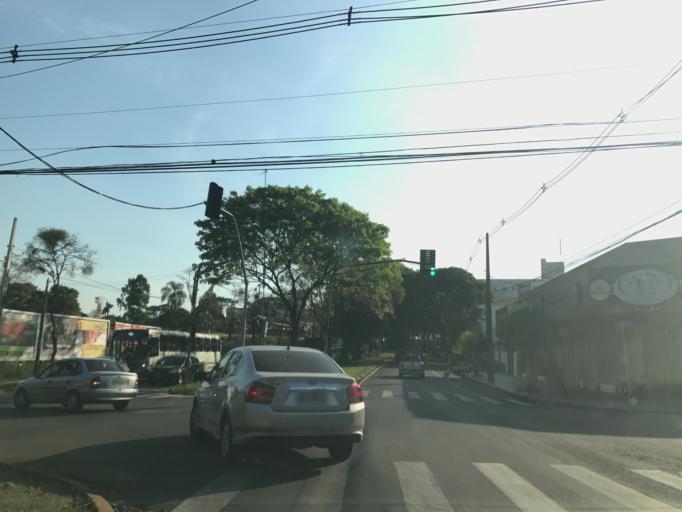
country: BR
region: Parana
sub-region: Maringa
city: Maringa
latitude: -23.4352
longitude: -51.9567
